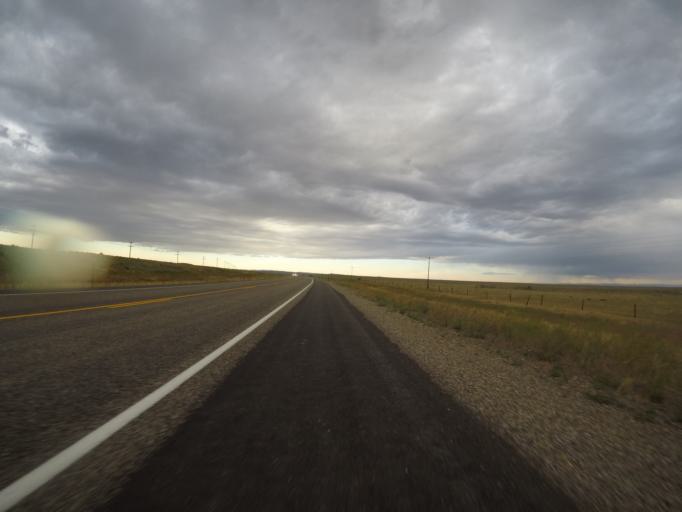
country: US
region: Wyoming
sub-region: Albany County
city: Laramie
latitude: 41.8124
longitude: -105.9897
